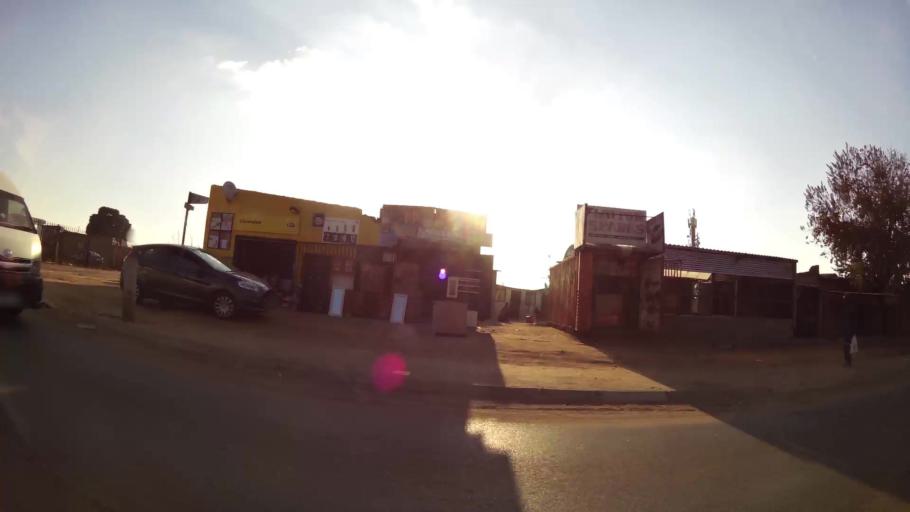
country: ZA
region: Gauteng
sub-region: Ekurhuleni Metropolitan Municipality
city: Tembisa
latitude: -25.9846
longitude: 28.2034
